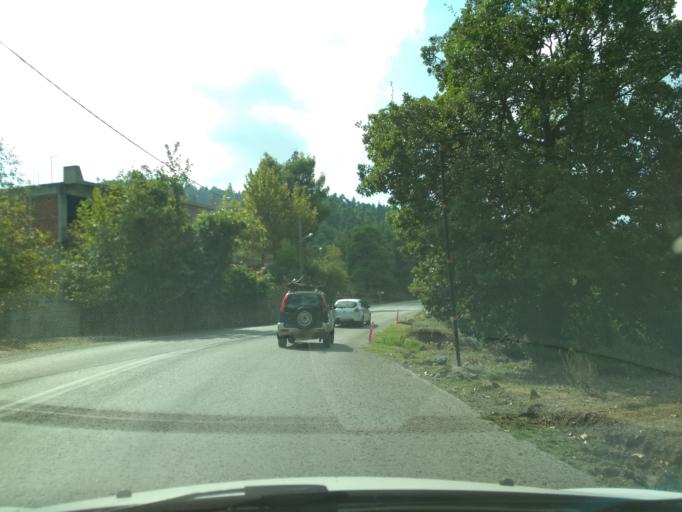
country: GR
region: Central Greece
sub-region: Nomos Evvoias
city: Politika
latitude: 38.6742
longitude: 23.5570
